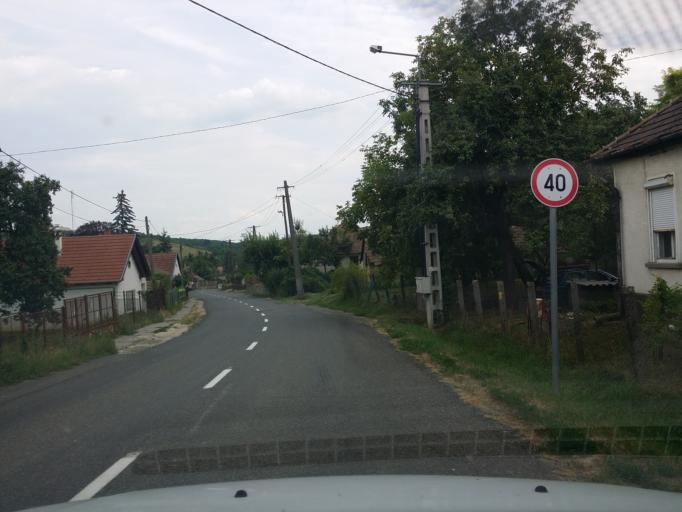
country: HU
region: Nograd
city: Bercel
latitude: 47.9138
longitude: 19.3742
